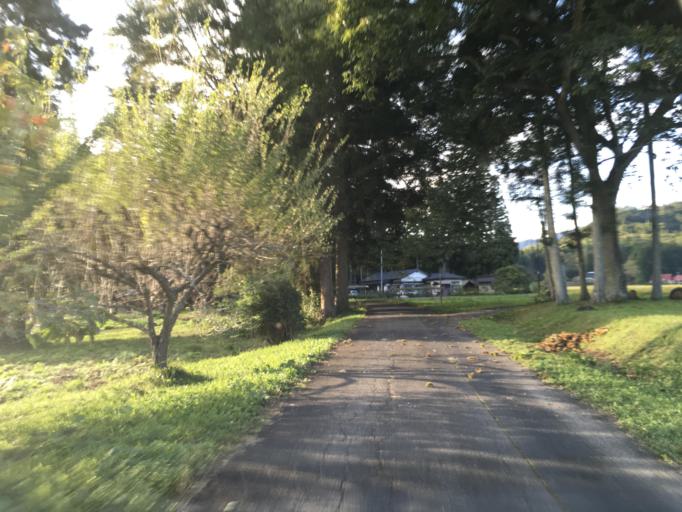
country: JP
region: Iwate
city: Ichinoseki
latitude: 38.9747
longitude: 140.9541
